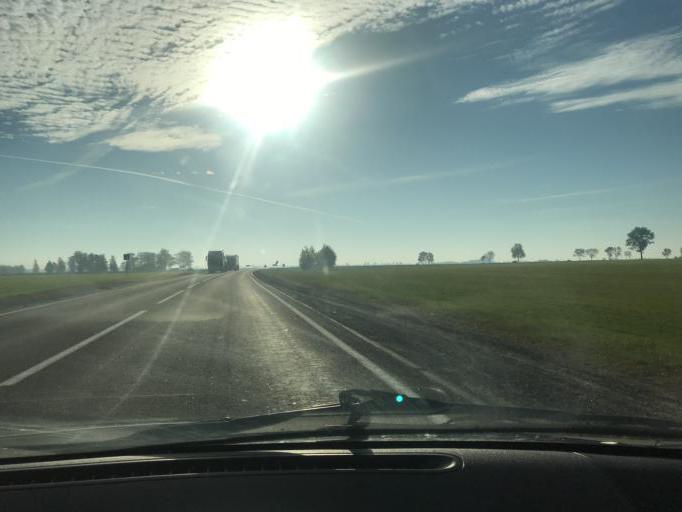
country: BY
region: Brest
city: Drahichyn
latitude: 52.2061
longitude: 25.2235
